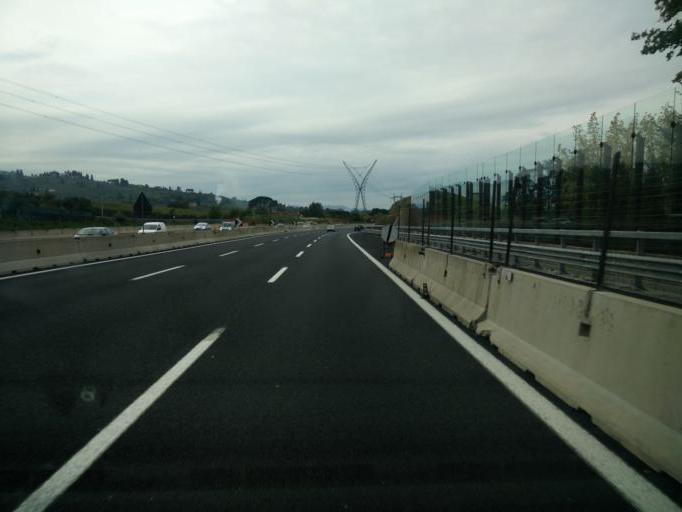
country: IT
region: Tuscany
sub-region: Province of Florence
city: Scandicci
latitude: 43.7448
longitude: 11.1768
